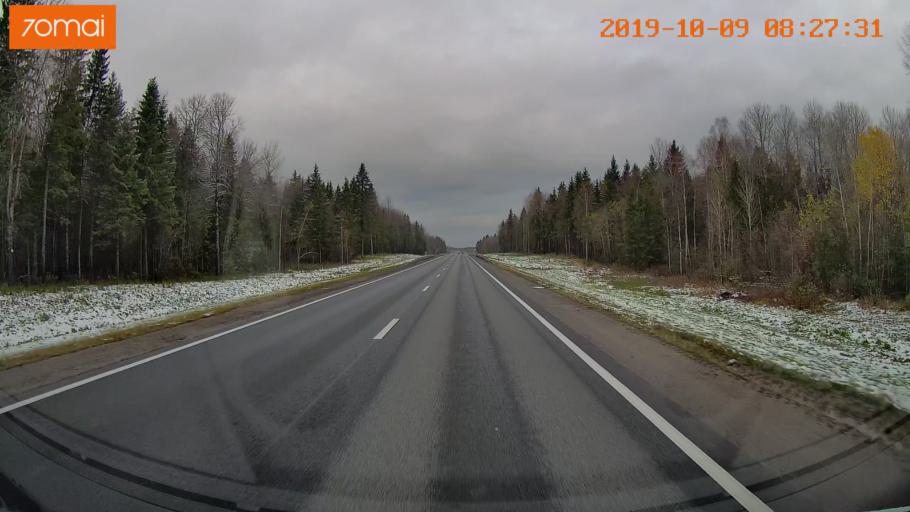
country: RU
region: Vologda
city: Gryazovets
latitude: 58.8048
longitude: 40.2474
